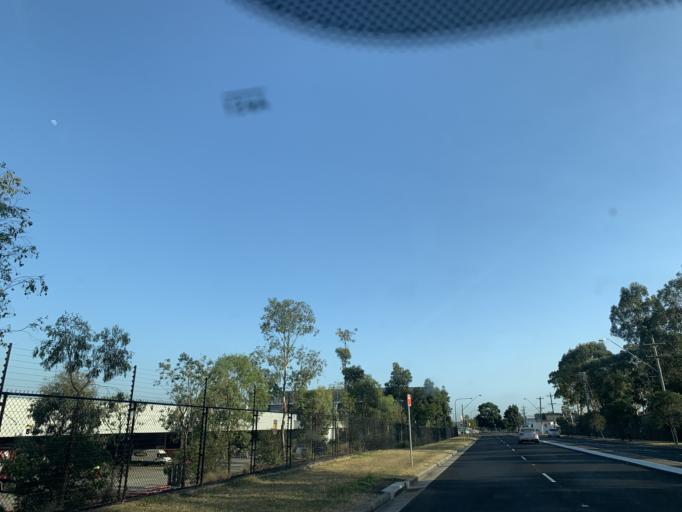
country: AU
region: New South Wales
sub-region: Blacktown
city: Doonside
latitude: -33.7980
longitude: 150.8706
